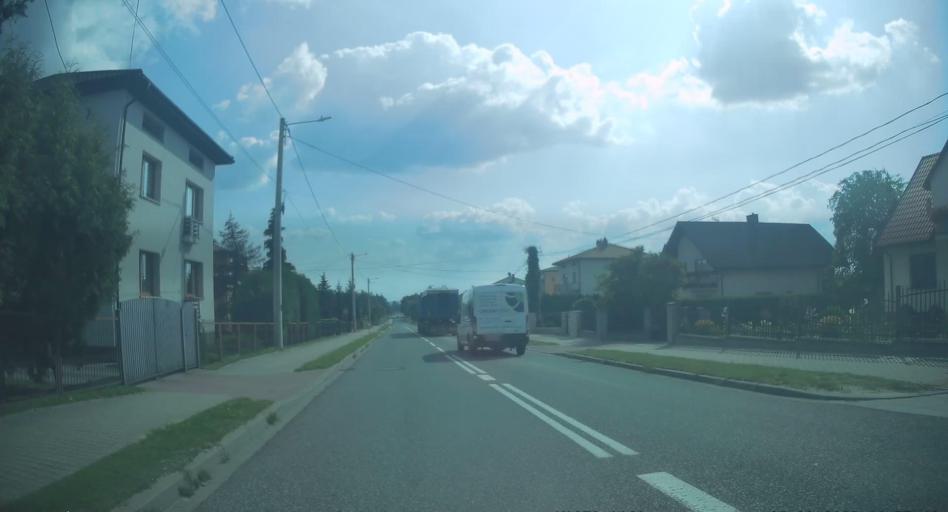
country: PL
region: Swietokrzyskie
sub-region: Powiat kielecki
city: Lopuszno
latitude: 50.9463
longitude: 20.2491
